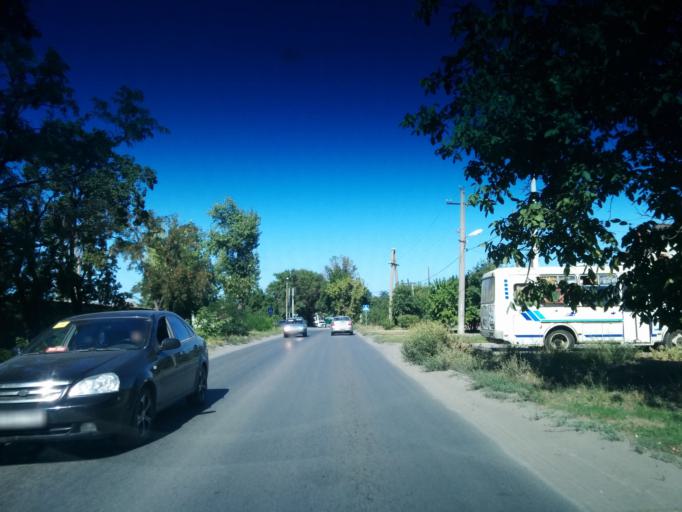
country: RU
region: Rostov
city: Shakhty
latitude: 47.7038
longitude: 40.2279
